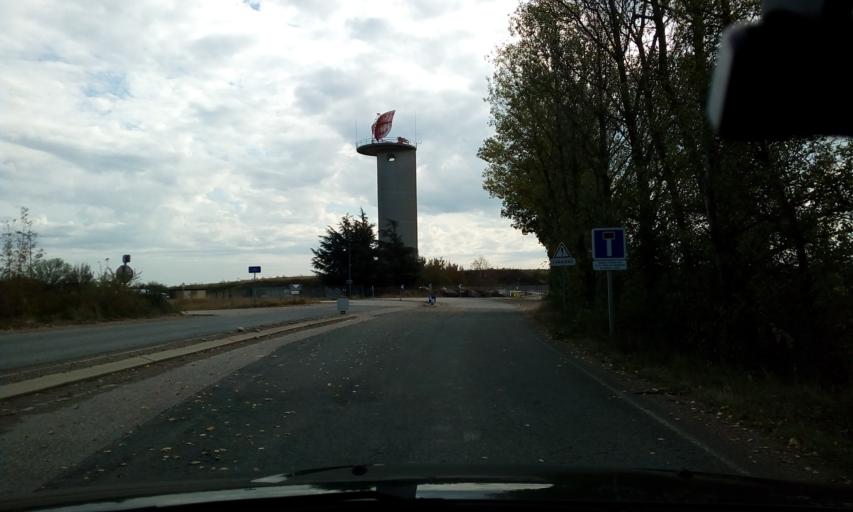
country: FR
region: Rhone-Alpes
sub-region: Departement de l'Isere
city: Grenay
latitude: 45.6973
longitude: 5.0804
